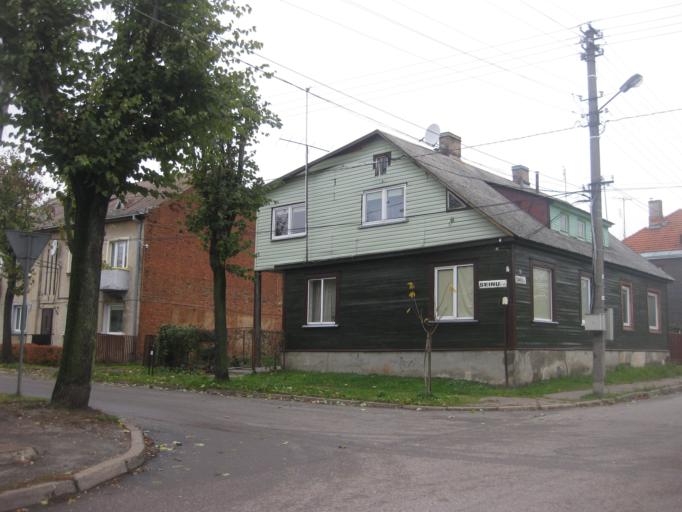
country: LT
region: Kauno apskritis
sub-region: Kaunas
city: Kaunas
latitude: 54.9065
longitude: 23.9150
